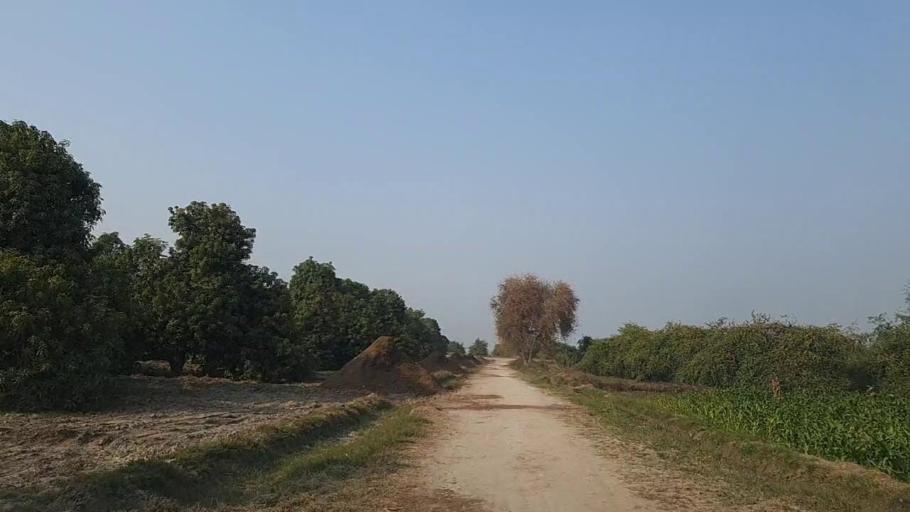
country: PK
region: Sindh
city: Sann
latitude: 26.1104
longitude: 68.1616
